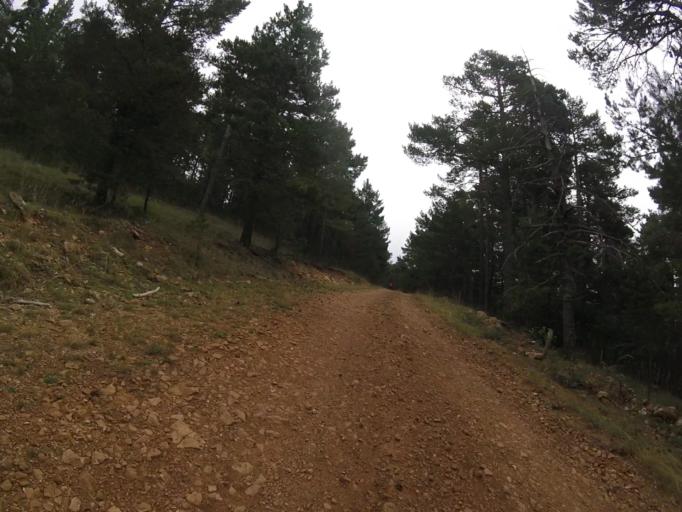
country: ES
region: Aragon
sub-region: Provincia de Teruel
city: Valdelinares
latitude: 40.3606
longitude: -0.6081
